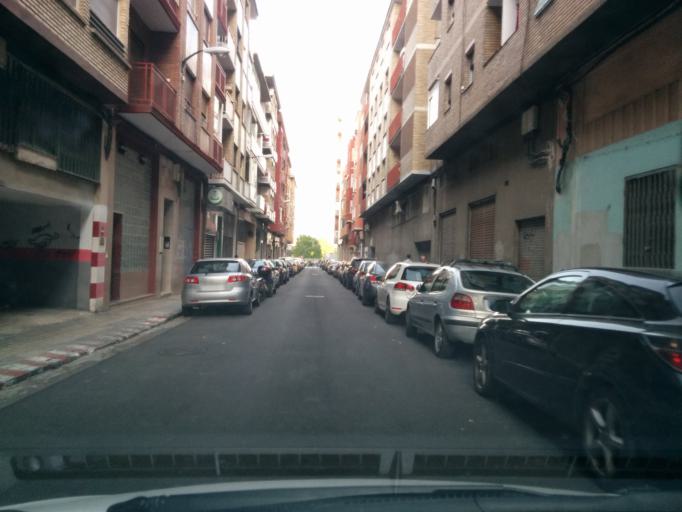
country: ES
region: Aragon
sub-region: Provincia de Zaragoza
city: Zaragoza
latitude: 41.6374
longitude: -0.8760
